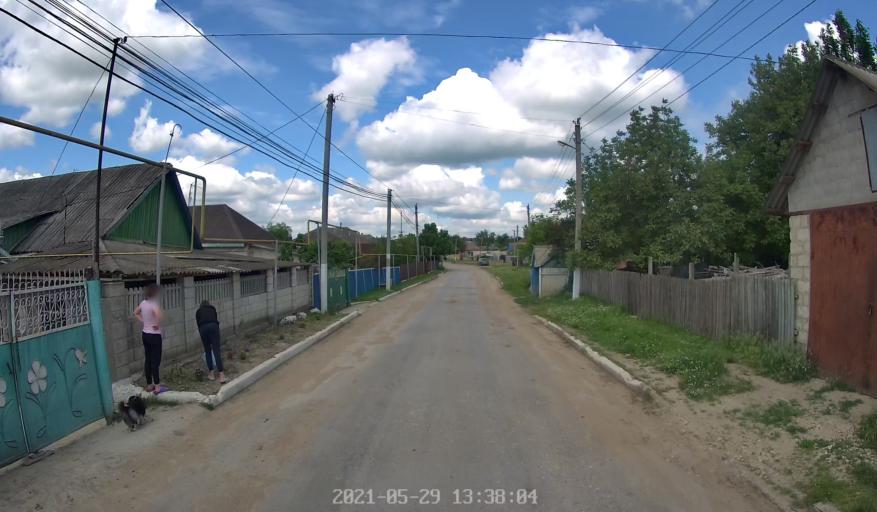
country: MD
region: Hincesti
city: Hincesti
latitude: 46.8296
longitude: 28.6765
